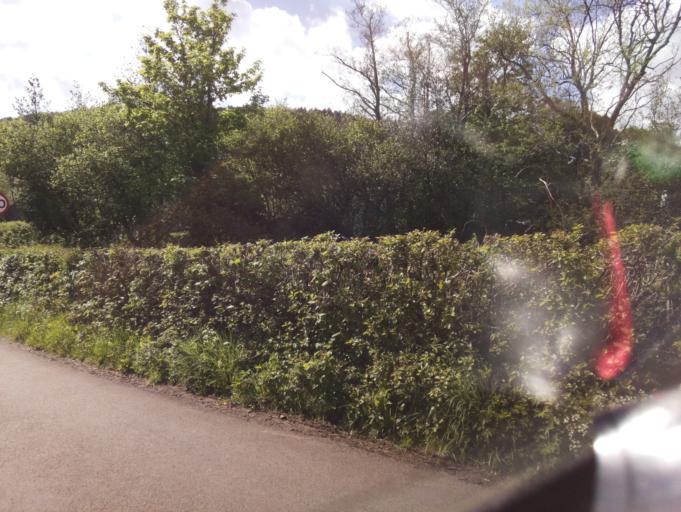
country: GB
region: Wales
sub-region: Caerphilly County Borough
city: Machen
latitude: 51.5793
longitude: -3.1245
